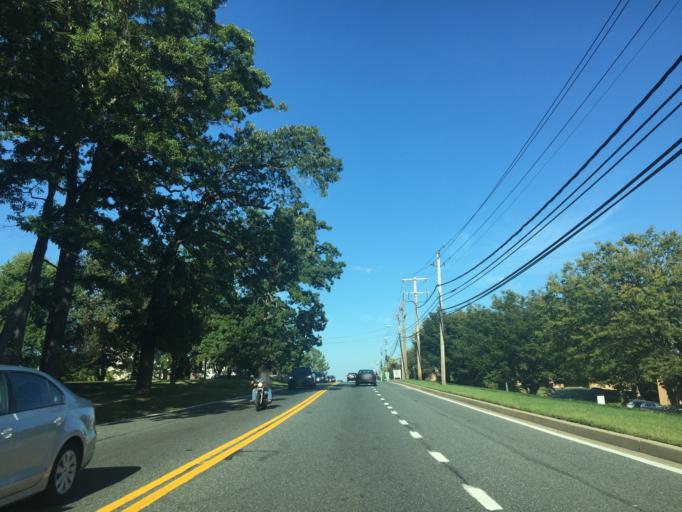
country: US
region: Maryland
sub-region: Baltimore County
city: Rossville
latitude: 39.3516
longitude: -76.4664
